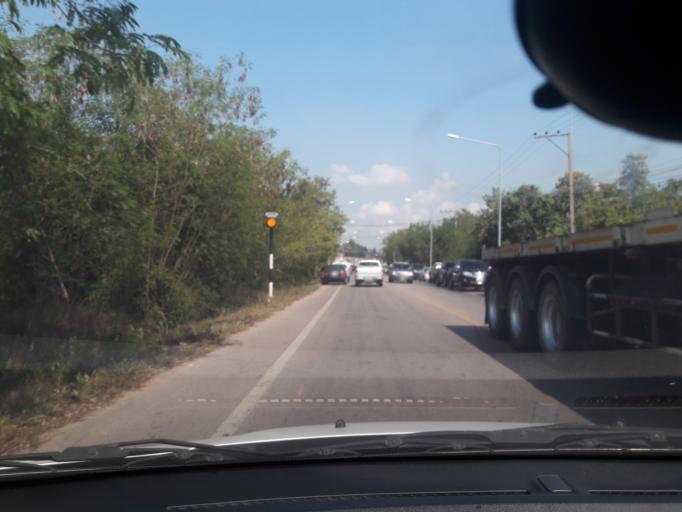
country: TH
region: Lampang
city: Lampang
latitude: 18.2268
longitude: 99.4906
